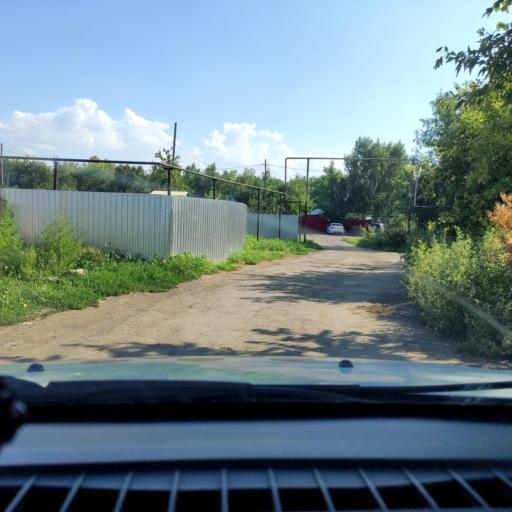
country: RU
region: Samara
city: Smyshlyayevka
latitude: 53.2070
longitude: 50.3287
